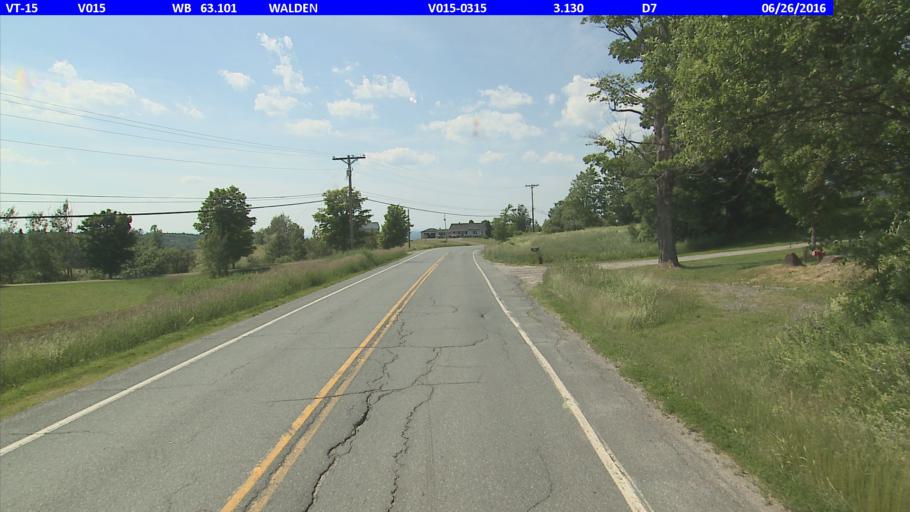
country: US
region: Vermont
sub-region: Caledonia County
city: Hardwick
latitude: 44.4555
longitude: -72.2613
